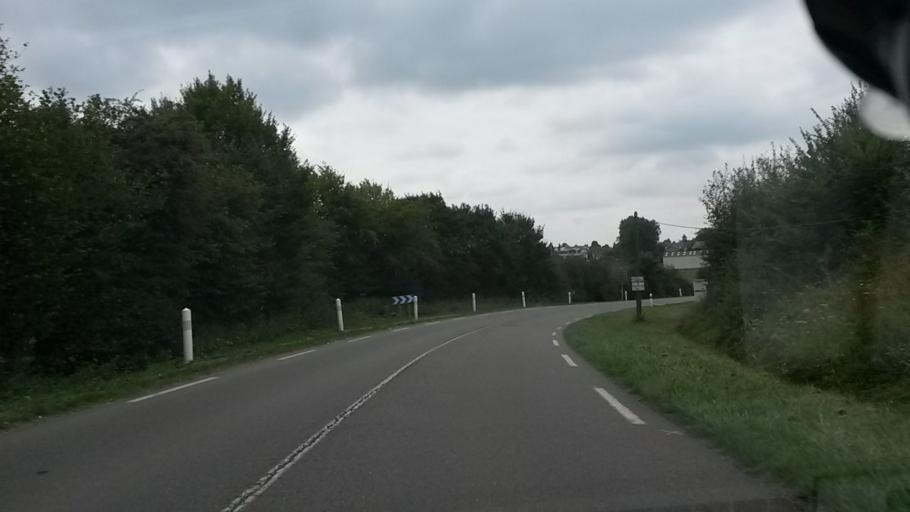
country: FR
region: Haute-Normandie
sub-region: Departement de la Seine-Maritime
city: Forges-les-Eaux
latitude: 49.6178
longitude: 1.5587
